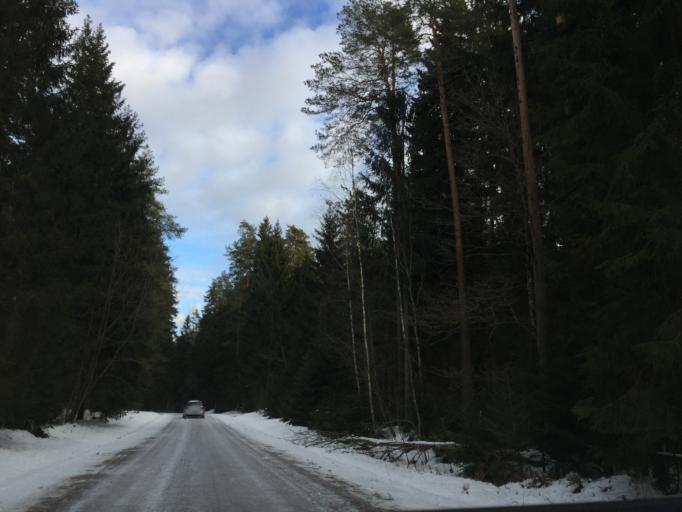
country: LV
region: Lielvarde
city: Lielvarde
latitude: 56.5625
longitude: 24.8025
